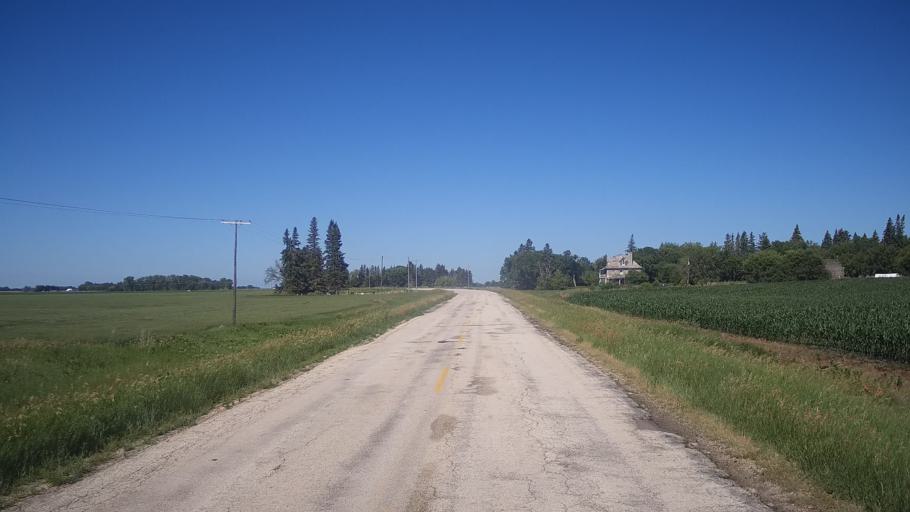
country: CA
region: Manitoba
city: Portage la Prairie
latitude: 50.0437
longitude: -98.0539
